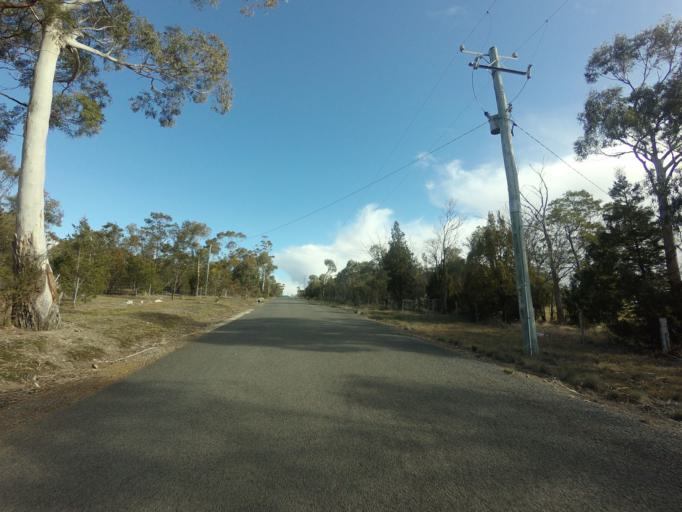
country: AU
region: Tasmania
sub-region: Sorell
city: Sorell
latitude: -42.3034
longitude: 147.9928
